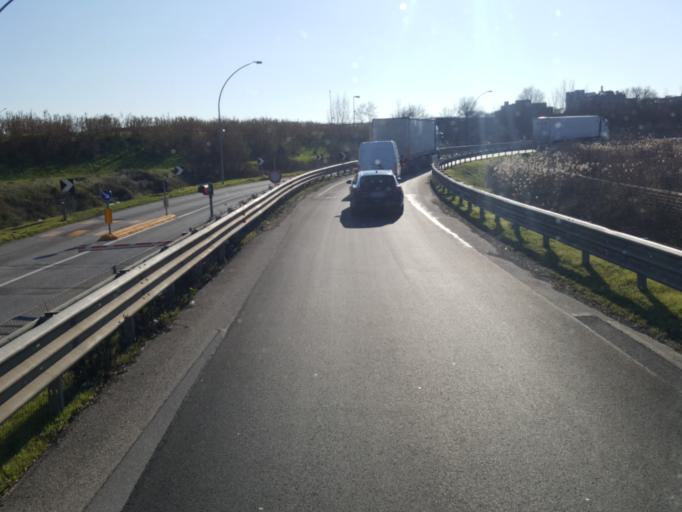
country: IT
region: Tuscany
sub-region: Province of Florence
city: Sesto Fiorentino
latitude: 43.8142
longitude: 11.1843
